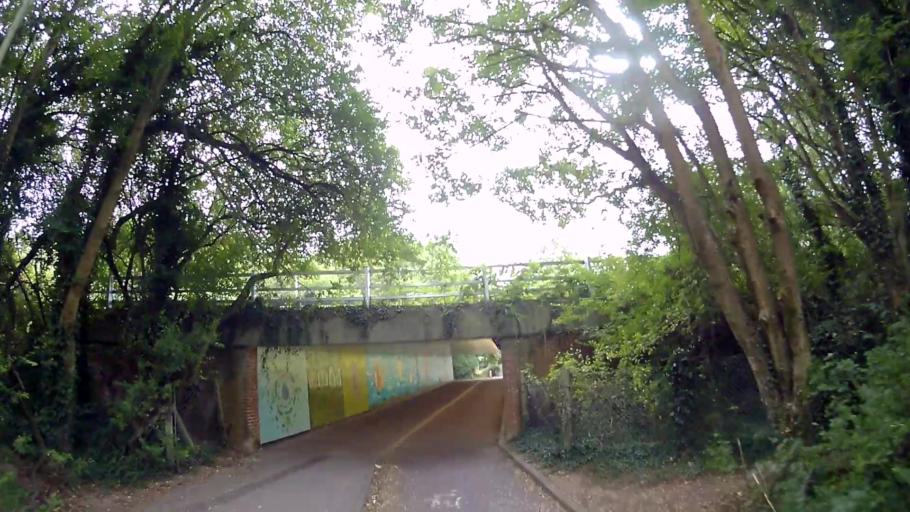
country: GB
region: England
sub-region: Hampshire
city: Basingstoke
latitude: 51.2542
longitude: -1.0990
